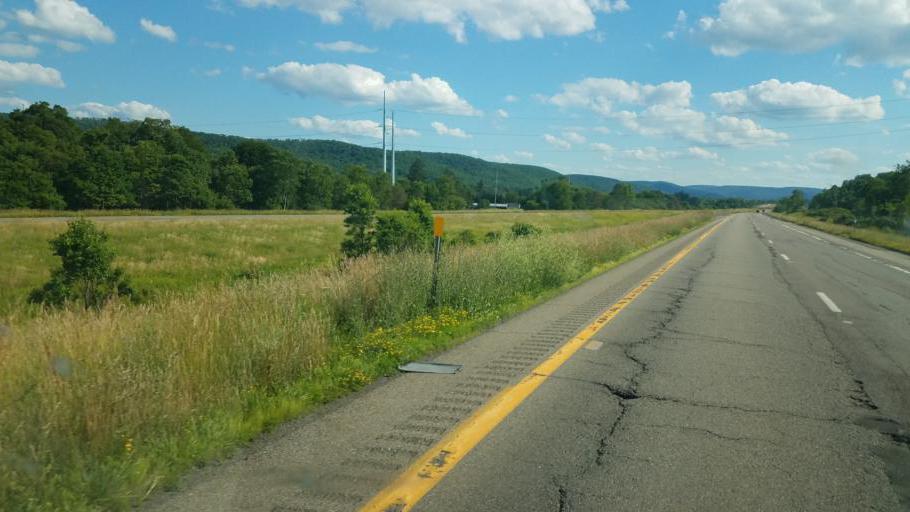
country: US
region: New York
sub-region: Cattaraugus County
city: Olean
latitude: 42.1463
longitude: -78.4082
